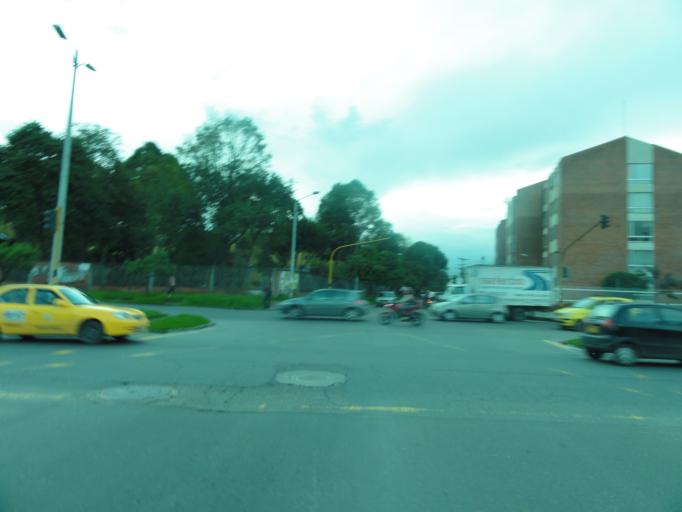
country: CO
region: Bogota D.C.
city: Bogota
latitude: 4.6512
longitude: -74.0843
